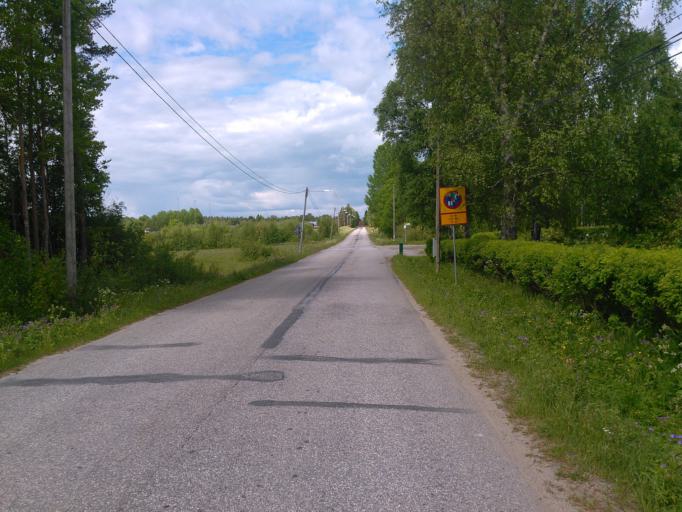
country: SE
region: Vaesterbotten
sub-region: Umea Kommun
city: Ersmark
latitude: 63.8782
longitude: 20.3201
